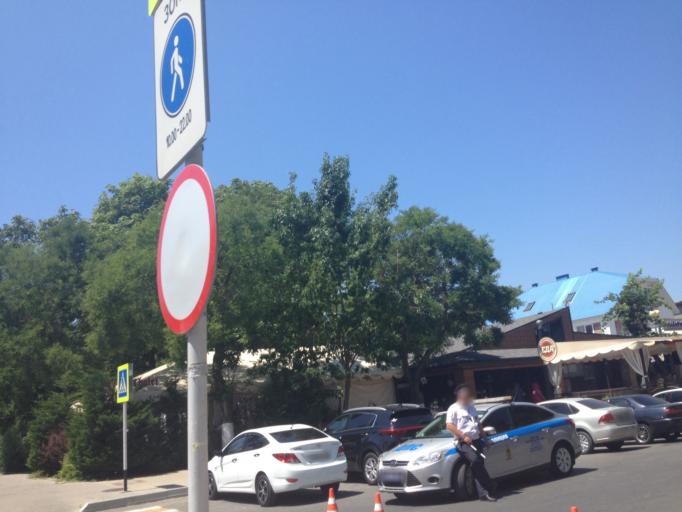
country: RU
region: Krasnodarskiy
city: Anapa
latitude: 44.8955
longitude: 37.3175
